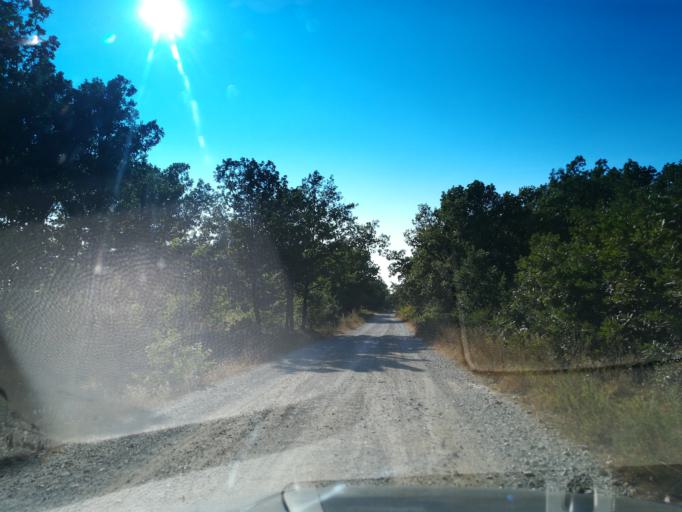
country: BG
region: Khaskovo
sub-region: Obshtina Mineralni Bani
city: Mineralni Bani
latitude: 41.9712
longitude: 25.3264
